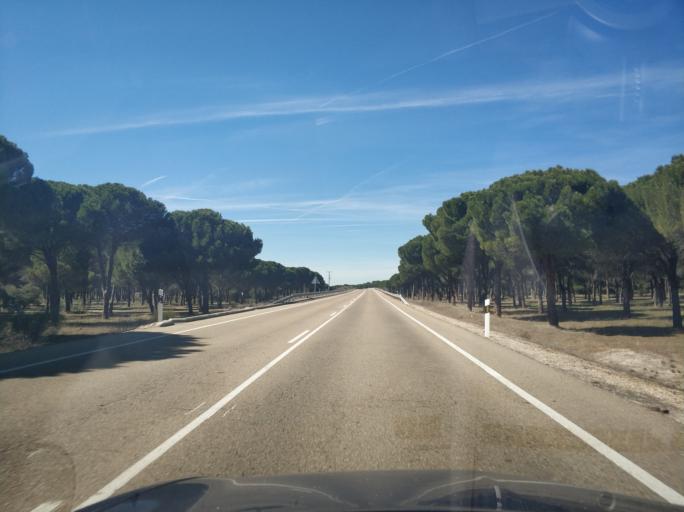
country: ES
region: Castille and Leon
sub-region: Provincia de Valladolid
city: Viana de Cega
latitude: 41.5327
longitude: -4.7318
